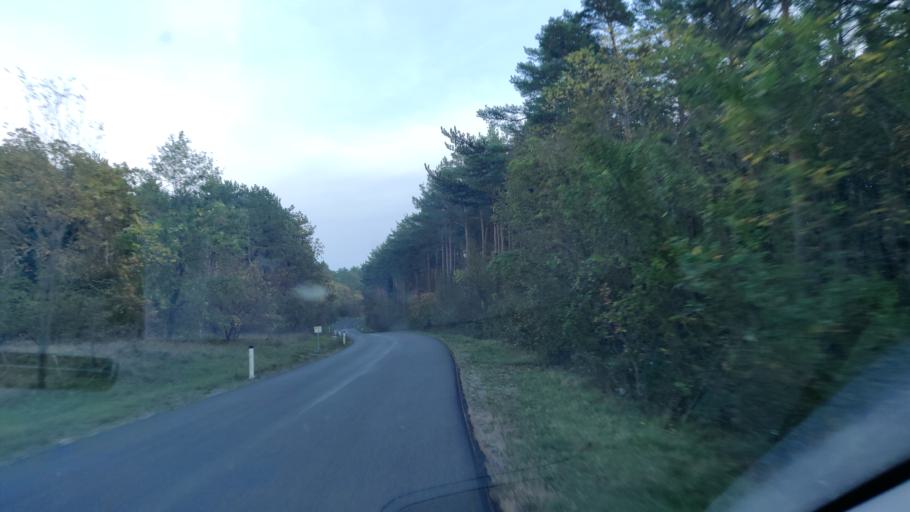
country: SI
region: Sezana
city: Sezana
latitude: 45.7736
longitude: 13.8744
